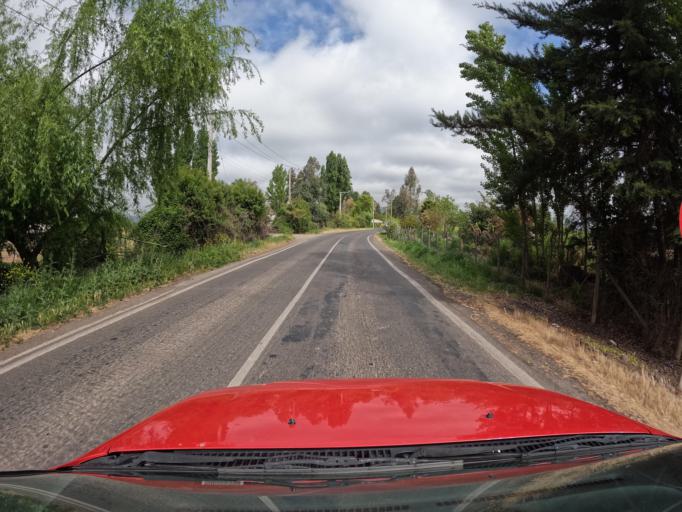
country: CL
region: O'Higgins
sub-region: Provincia de Colchagua
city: Santa Cruz
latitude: -34.6781
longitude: -71.3617
